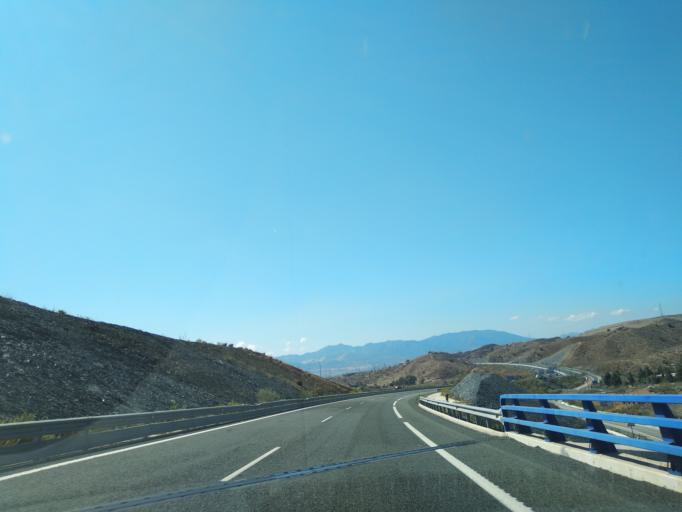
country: ES
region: Andalusia
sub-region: Provincia de Malaga
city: Malaga
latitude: 36.7541
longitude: -4.4892
